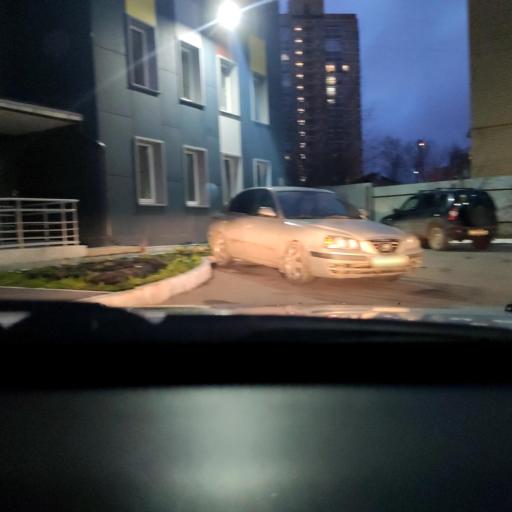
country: RU
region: Perm
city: Perm
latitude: 57.9907
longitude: 56.2204
